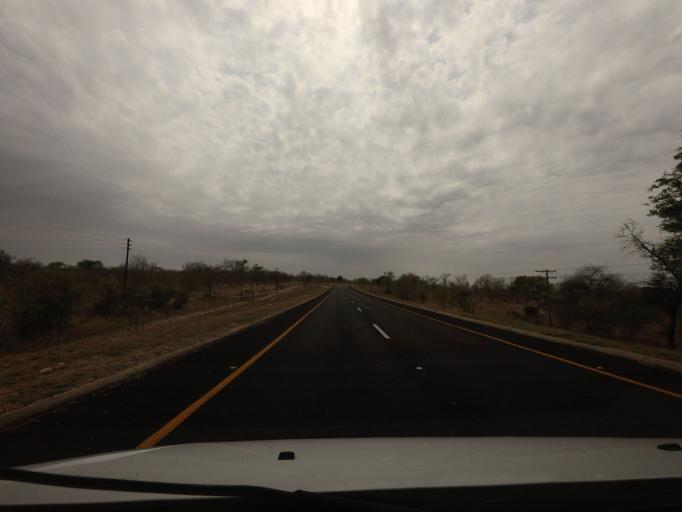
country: ZA
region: Limpopo
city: Thulamahashi
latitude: -24.5567
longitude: 31.1798
